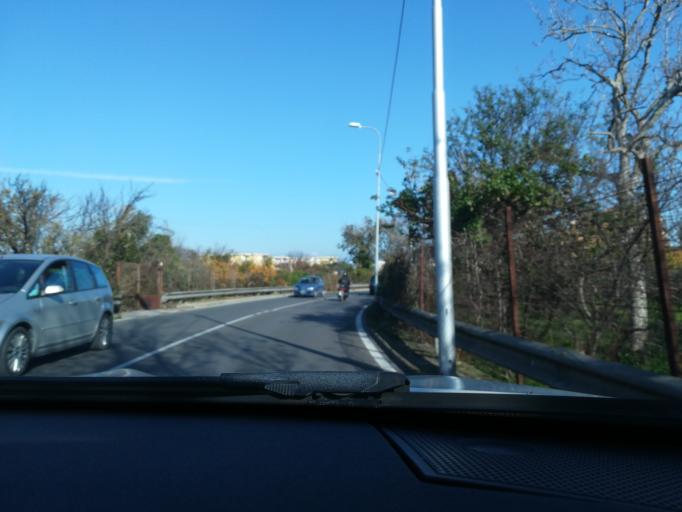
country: IT
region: Campania
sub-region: Provincia di Napoli
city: Sant'Anastasia
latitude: 40.8720
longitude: 14.3948
